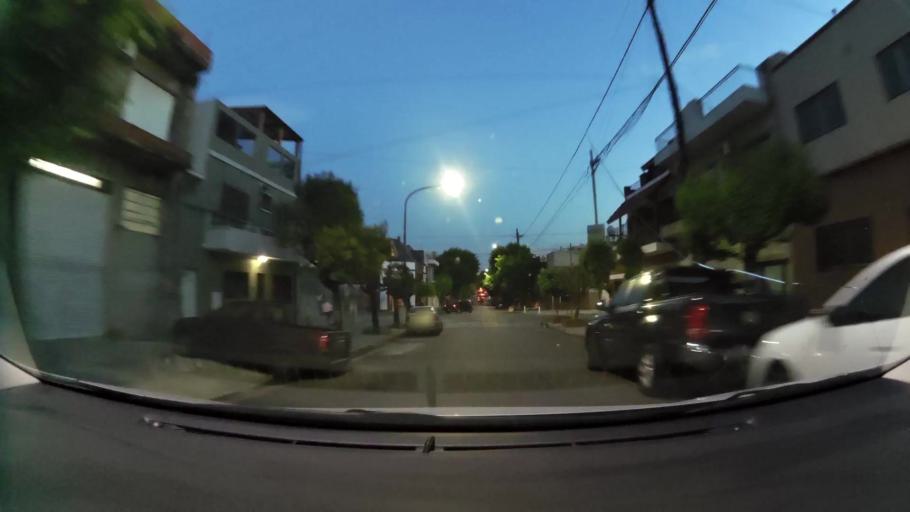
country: AR
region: Buenos Aires F.D.
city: Villa Lugano
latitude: -34.6861
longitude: -58.4807
